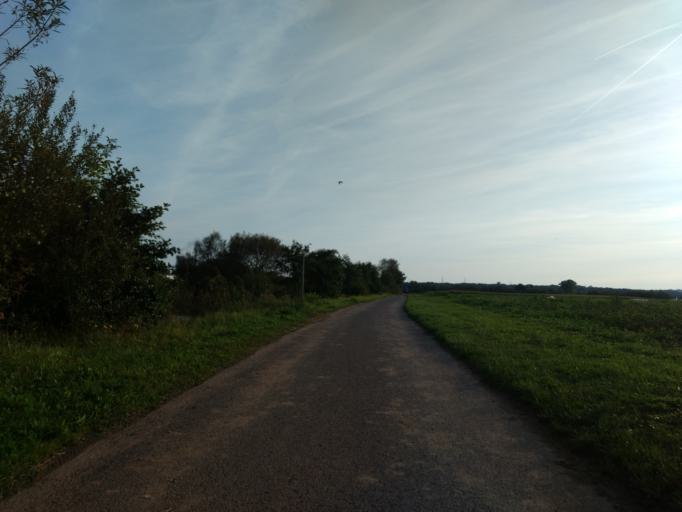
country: DE
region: Saarland
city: Ensdorf
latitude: 49.3143
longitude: 6.7718
